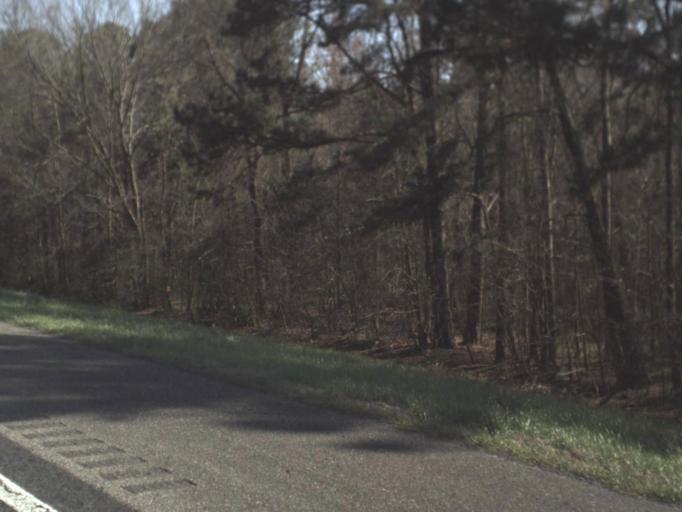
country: US
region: Florida
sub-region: Gadsden County
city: Quincy
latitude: 30.5432
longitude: -84.6096
